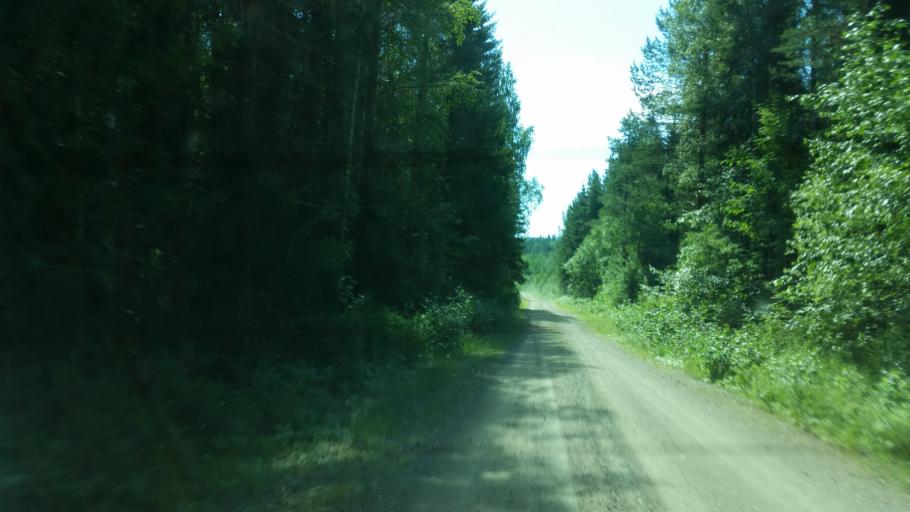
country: SE
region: Vaesternorrland
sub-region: Ange Kommun
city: Ange
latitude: 62.2244
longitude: 15.4041
